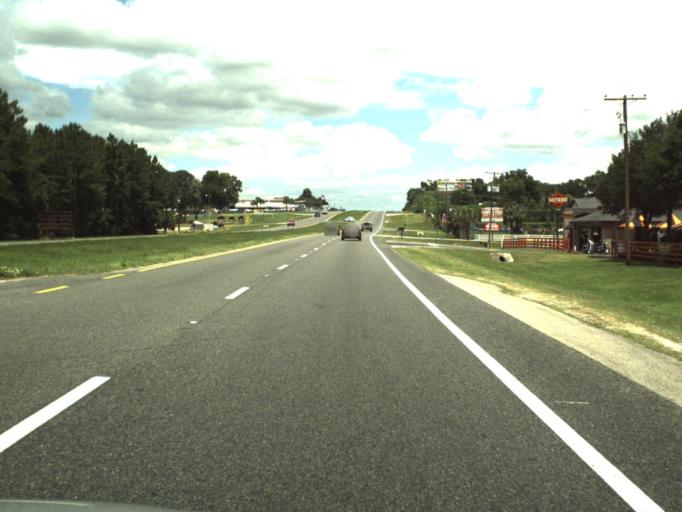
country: US
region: Florida
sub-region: Marion County
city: Ocala
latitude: 29.2410
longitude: -82.1520
